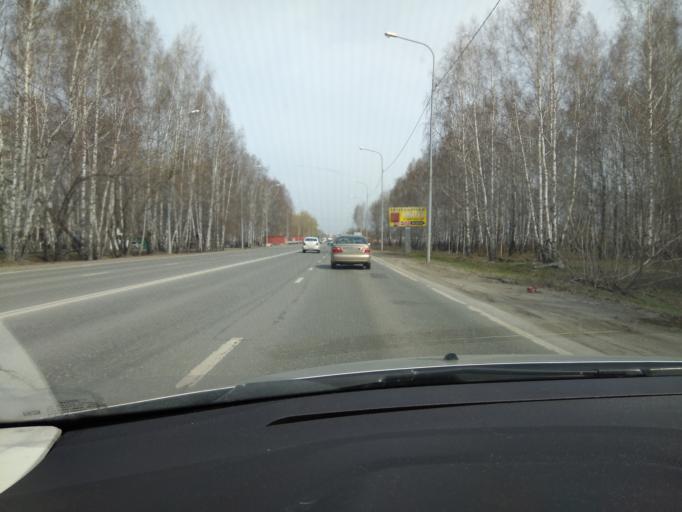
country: RU
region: Tjumen
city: Melioratorov
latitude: 57.1804
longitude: 65.5914
